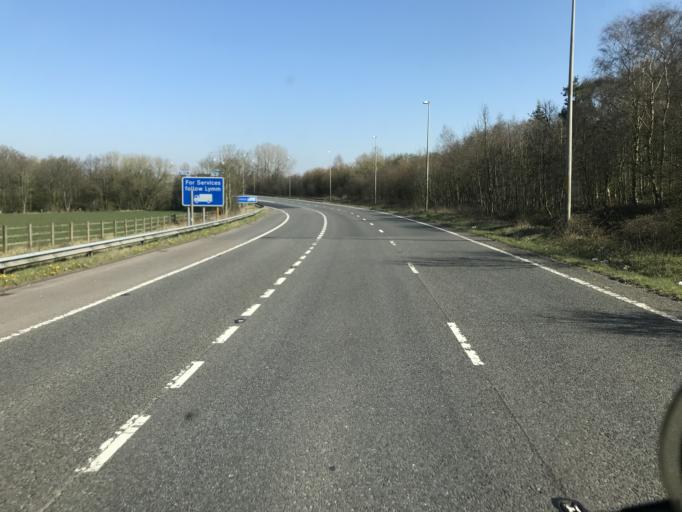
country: GB
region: England
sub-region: Warrington
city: Appleton Thorn
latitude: 53.3525
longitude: -2.5091
